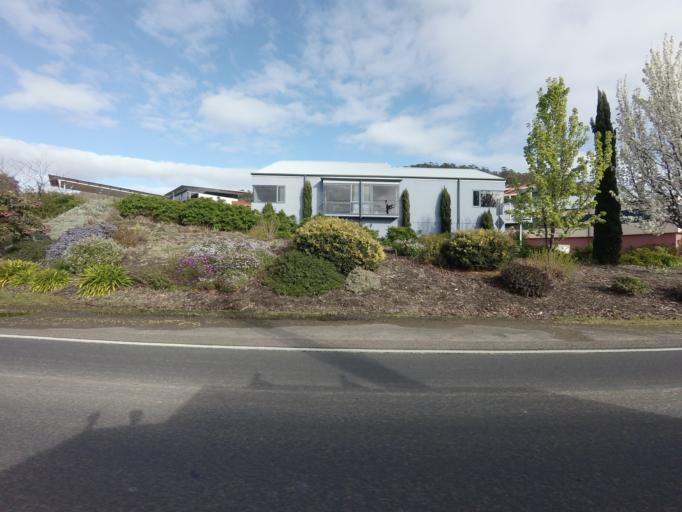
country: AU
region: Tasmania
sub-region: Huon Valley
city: Franklin
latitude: -43.0813
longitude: 147.0169
